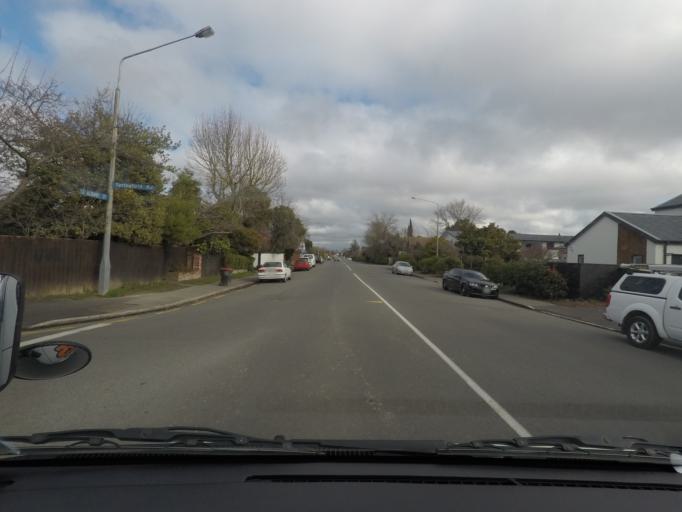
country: NZ
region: Canterbury
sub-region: Christchurch City
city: Christchurch
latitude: -43.5095
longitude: 172.6300
